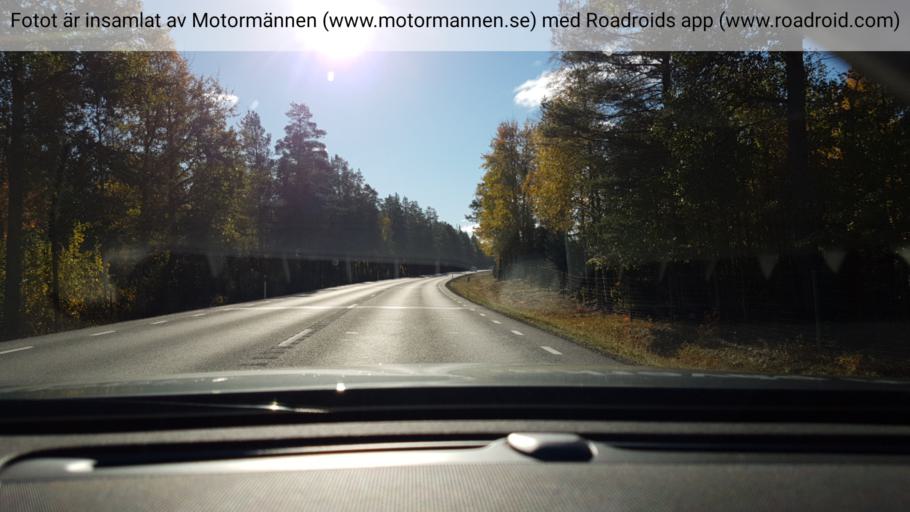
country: SE
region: Vaesterbotten
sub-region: Skelleftea Kommun
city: Burea
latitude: 64.5867
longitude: 21.2175
